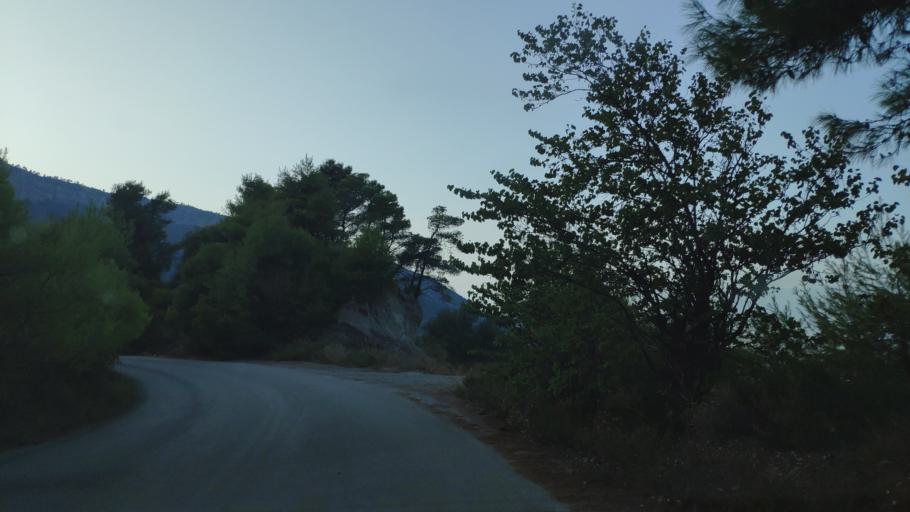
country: GR
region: West Greece
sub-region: Nomos Achaias
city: Aiyira
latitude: 38.0987
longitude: 22.4021
